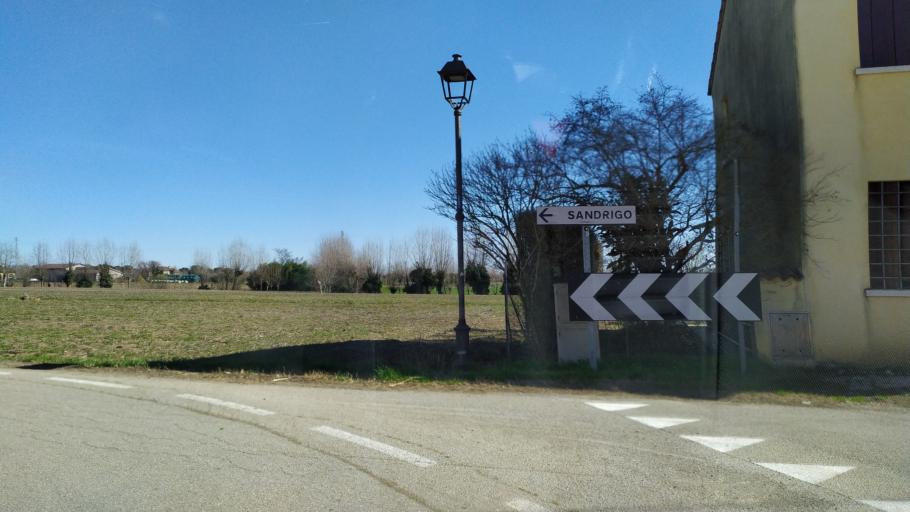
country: IT
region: Veneto
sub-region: Provincia di Vicenza
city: Vigardolo
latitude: 45.6279
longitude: 11.6011
